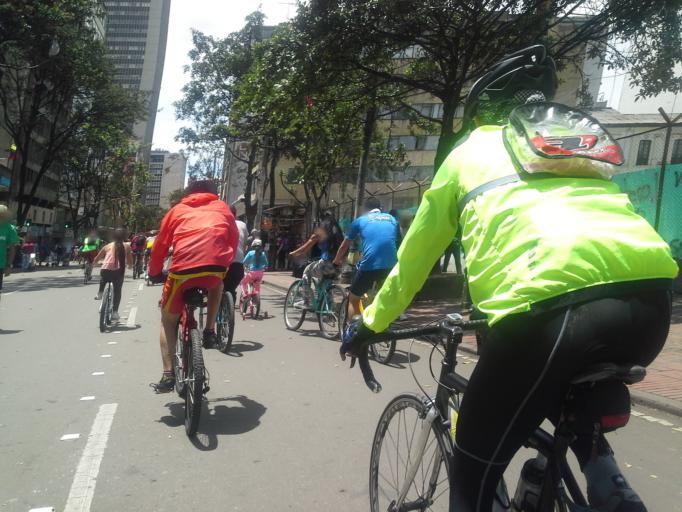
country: CO
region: Bogota D.C.
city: Bogota
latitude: 4.6050
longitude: -74.0718
